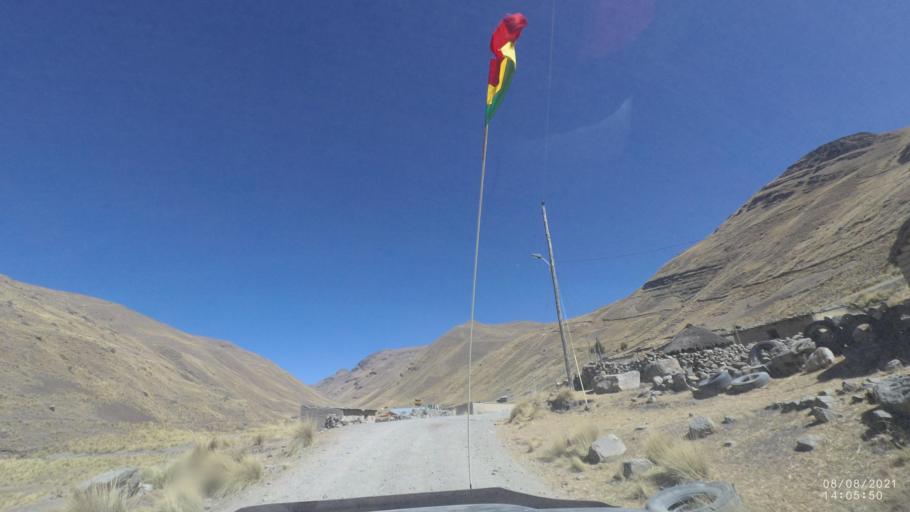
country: BO
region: Cochabamba
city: Sipe Sipe
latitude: -17.1202
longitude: -66.4405
